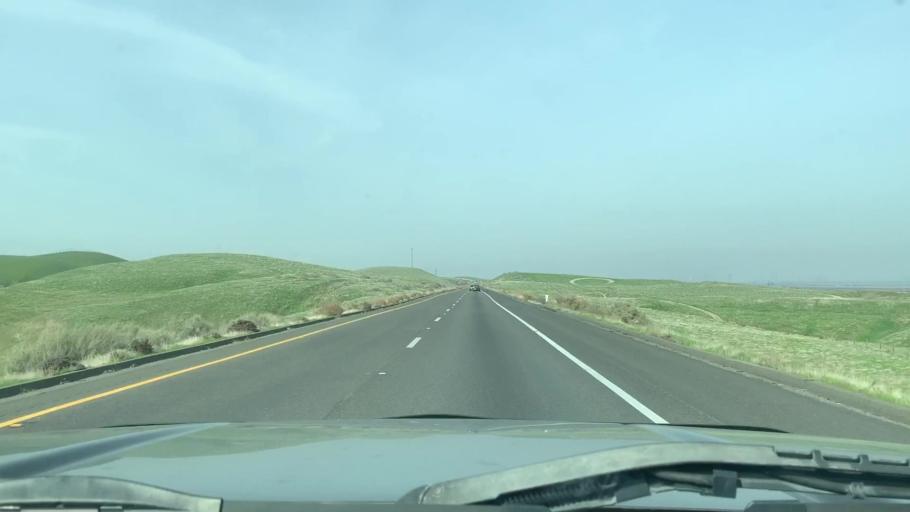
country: US
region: California
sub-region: Kings County
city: Kettleman City
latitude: 36.0002
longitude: -119.9779
